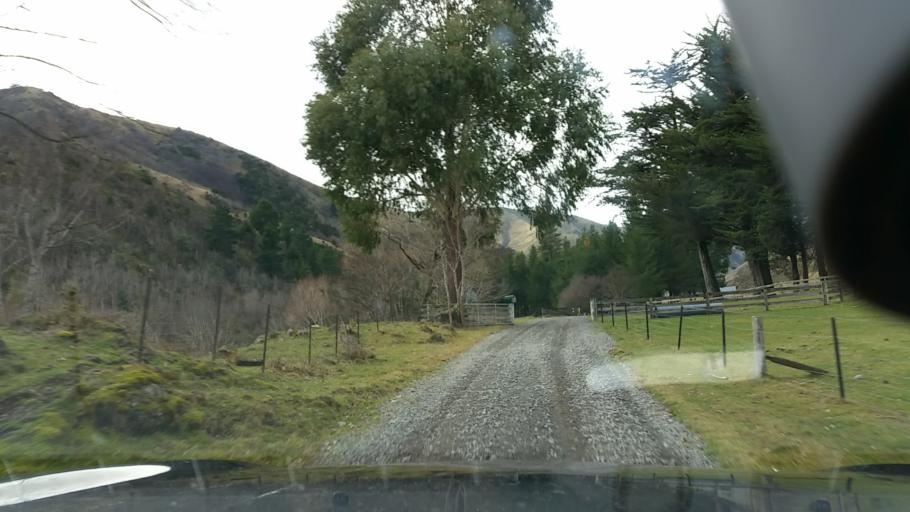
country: NZ
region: Tasman
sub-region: Tasman District
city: Brightwater
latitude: -41.7362
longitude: 173.4211
